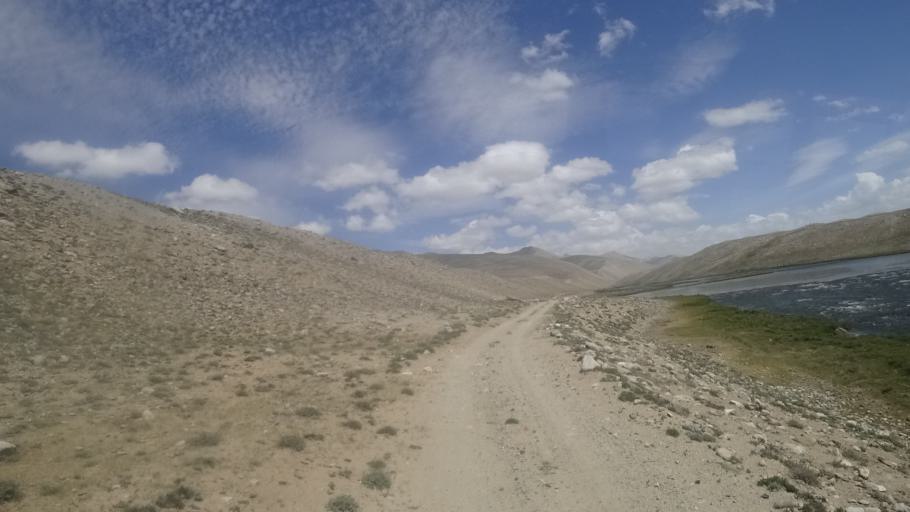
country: TJ
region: Gorno-Badakhshan
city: Murghob
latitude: 37.4695
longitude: 73.4279
